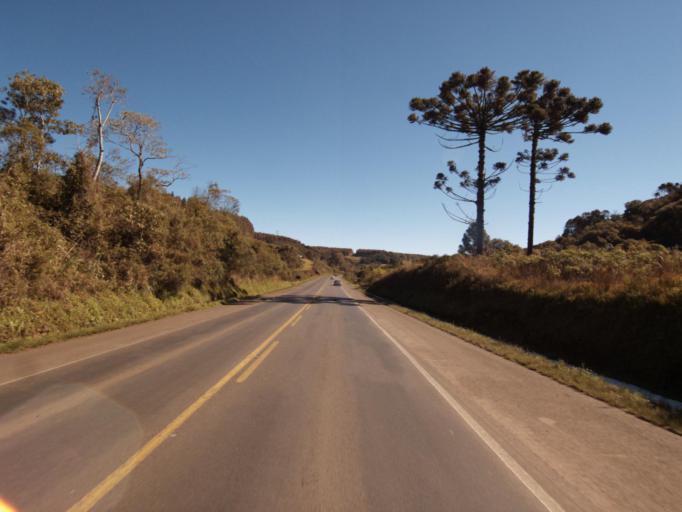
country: BR
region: Santa Catarina
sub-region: Concordia
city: Concordia
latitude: -26.8861
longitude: -52.0017
